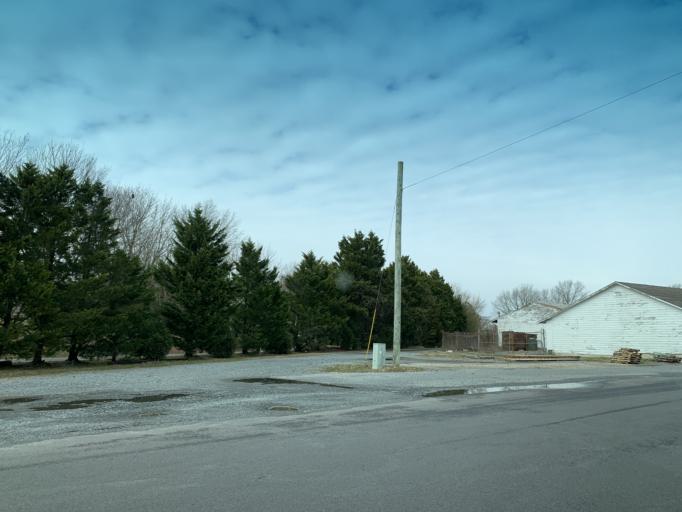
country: US
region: Maryland
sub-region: Worcester County
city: Berlin
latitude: 38.3270
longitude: -75.2223
